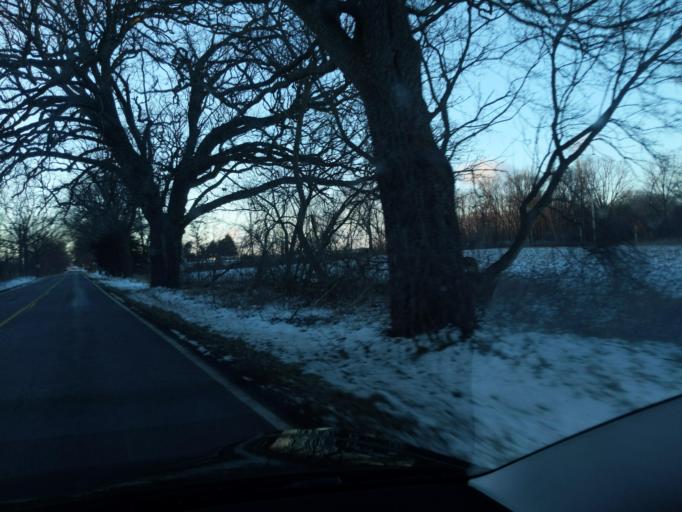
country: US
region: Michigan
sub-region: Ingham County
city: Stockbridge
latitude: 42.4484
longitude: -84.2478
